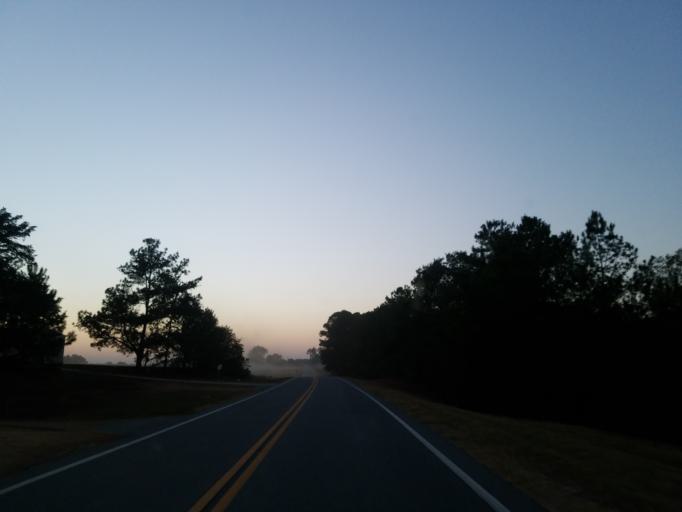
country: US
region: Georgia
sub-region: Wilcox County
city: Rochelle
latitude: 31.8156
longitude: -83.5104
